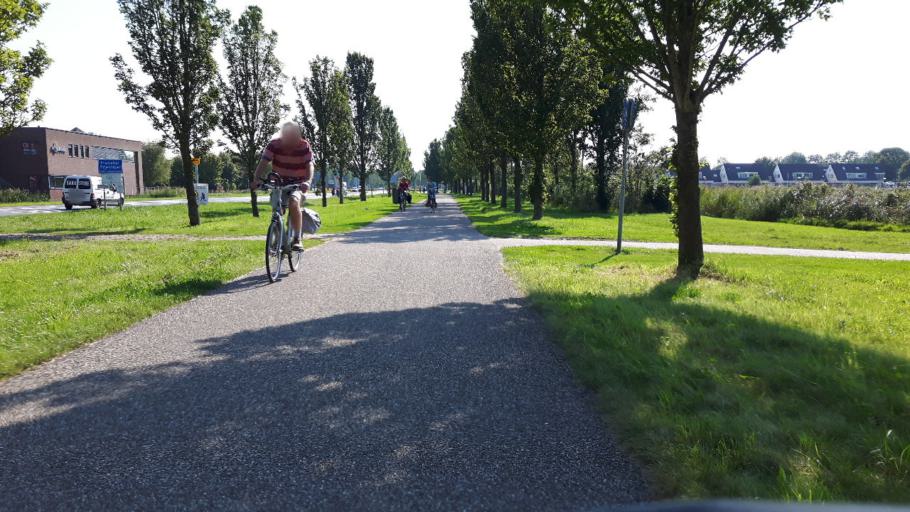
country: NL
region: Friesland
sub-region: Gemeente Franekeradeel
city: Franeker
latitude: 53.1989
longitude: 5.5411
